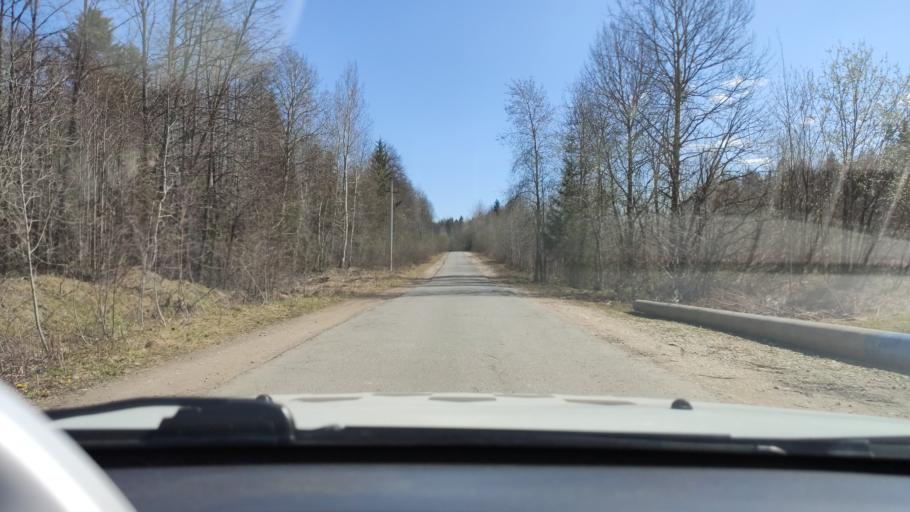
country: RU
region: Perm
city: Novyye Lyady
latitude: 58.0422
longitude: 56.6209
